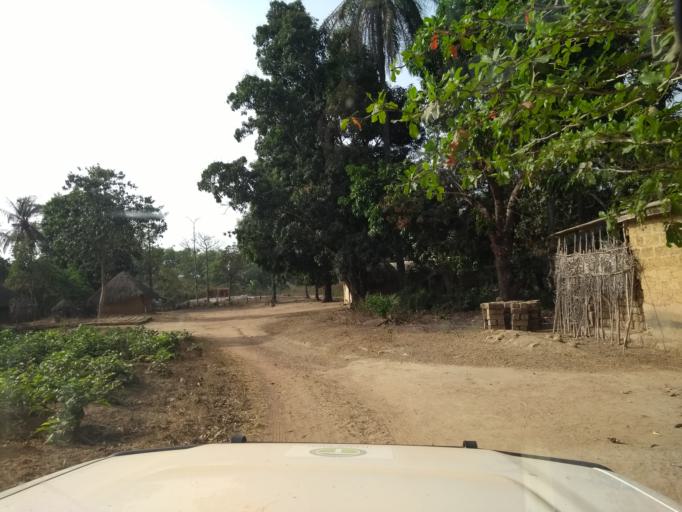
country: GN
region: Kindia
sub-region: Prefecture de Dubreka
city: Dubreka
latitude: 9.8218
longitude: -13.5549
